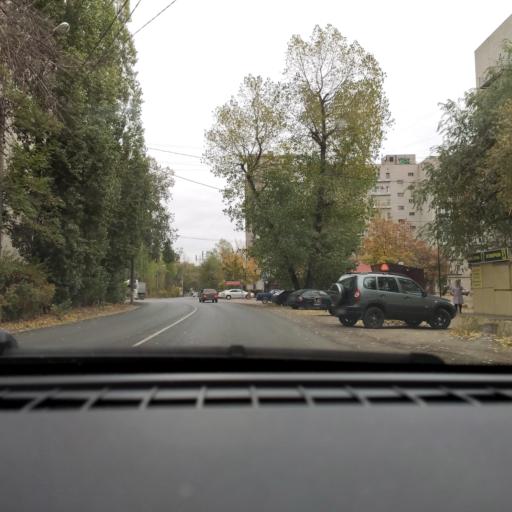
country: RU
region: Voronezj
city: Maslovka
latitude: 51.6373
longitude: 39.2690
